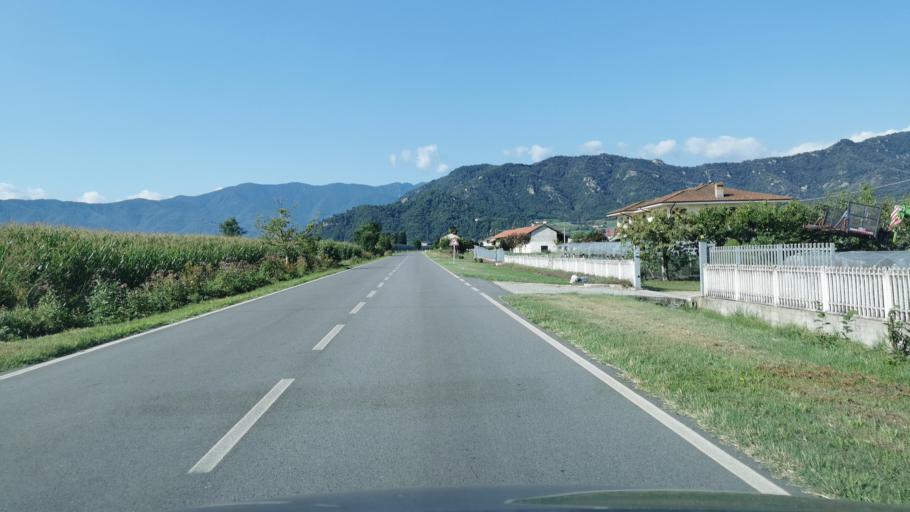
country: IT
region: Piedmont
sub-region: Provincia di Cuneo
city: Revello
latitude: 44.6748
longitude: 7.4055
